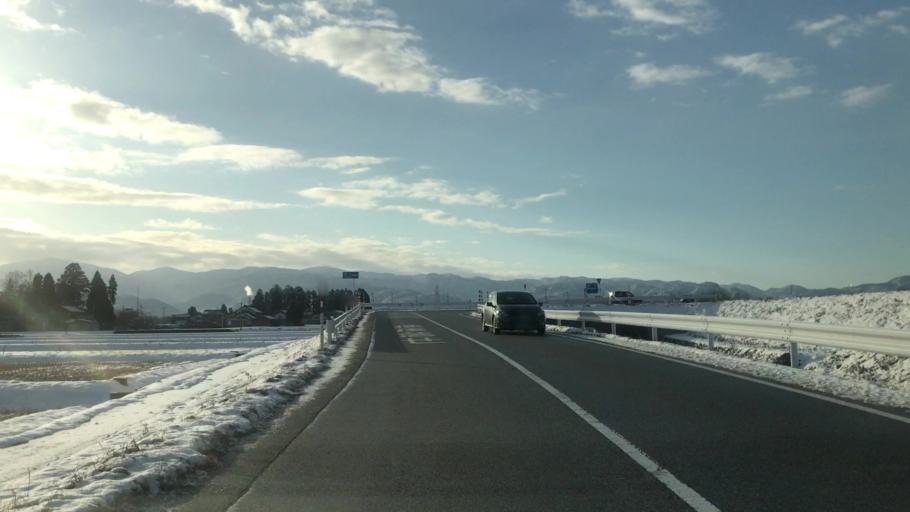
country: JP
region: Toyama
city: Toyama-shi
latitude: 36.6482
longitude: 137.2864
